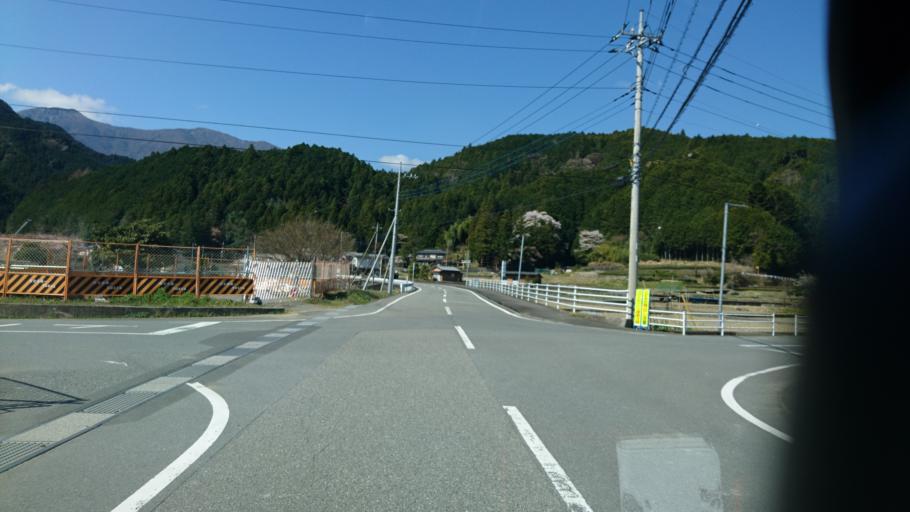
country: JP
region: Shizuoka
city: Fujinomiya
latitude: 35.2875
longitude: 138.4400
